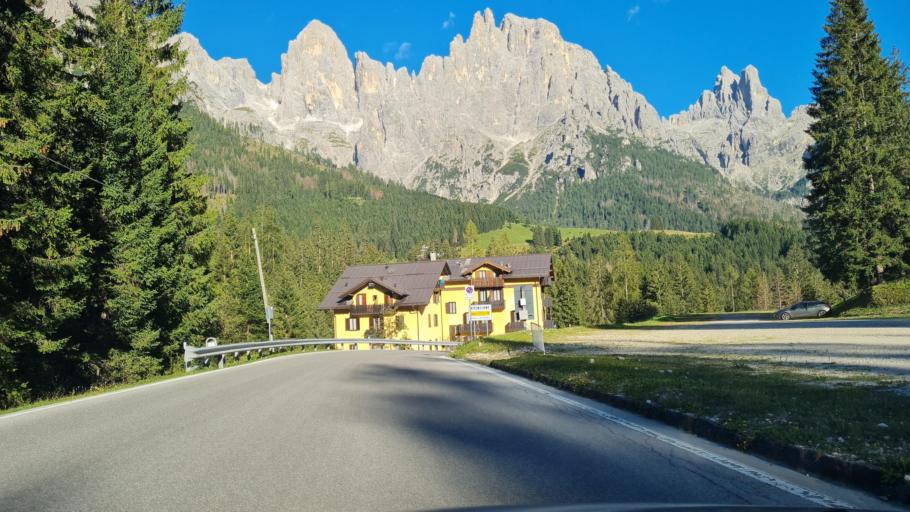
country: IT
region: Trentino-Alto Adige
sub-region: Provincia di Trento
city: Siror
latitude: 46.2547
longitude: 11.8008
